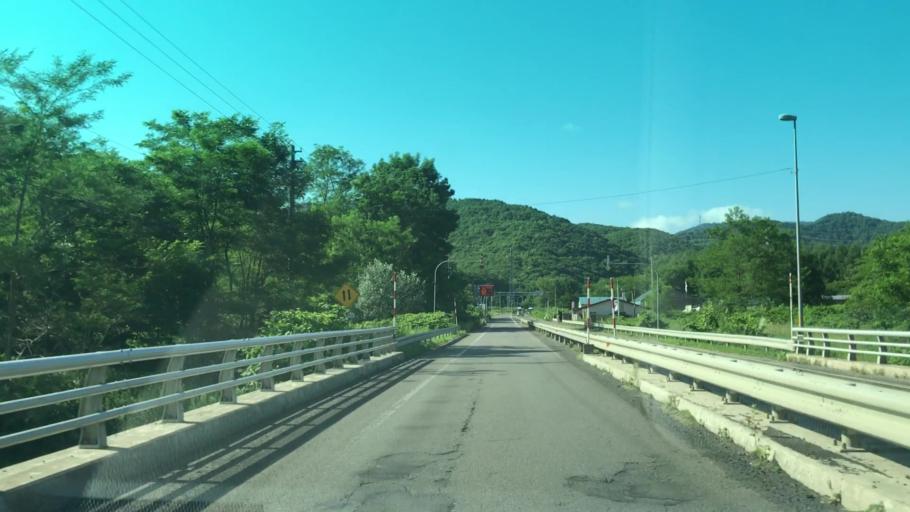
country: JP
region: Hokkaido
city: Iwanai
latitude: 43.0041
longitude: 140.6675
